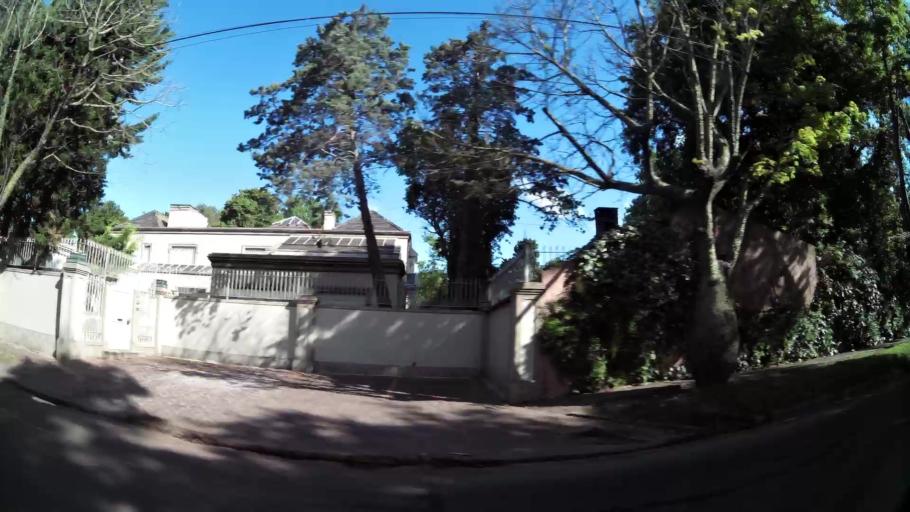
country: AR
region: Buenos Aires
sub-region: Partido de San Isidro
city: San Isidro
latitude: -34.4853
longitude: -58.5638
